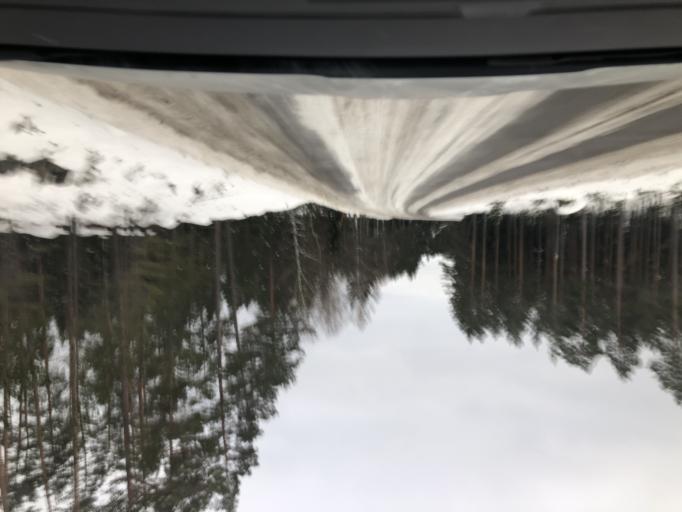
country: SE
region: OEstergoetland
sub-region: Atvidabergs Kommun
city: Atvidaberg
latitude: 58.1126
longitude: 15.9525
